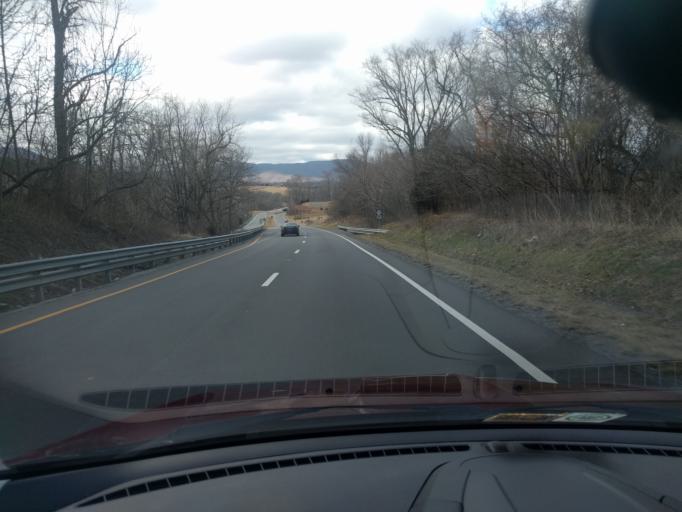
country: US
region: Virginia
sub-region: Botetourt County
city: Blue Ridge
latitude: 37.3680
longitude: -79.6930
